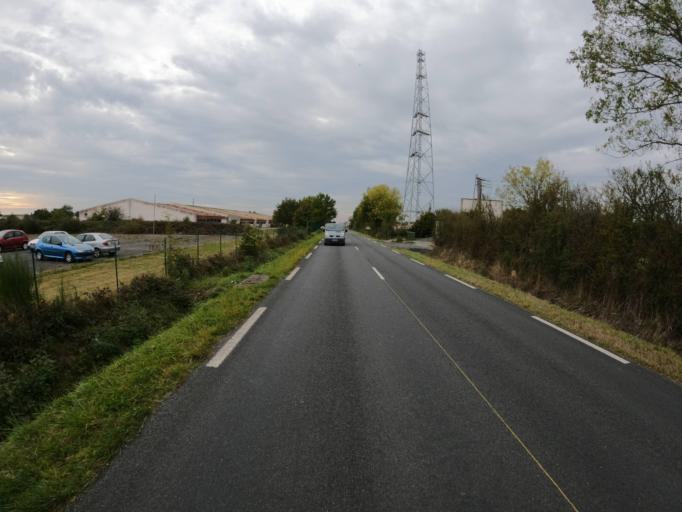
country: FR
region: Pays de la Loire
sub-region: Departement de la Loire-Atlantique
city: Getigne
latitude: 47.0759
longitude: -1.2339
